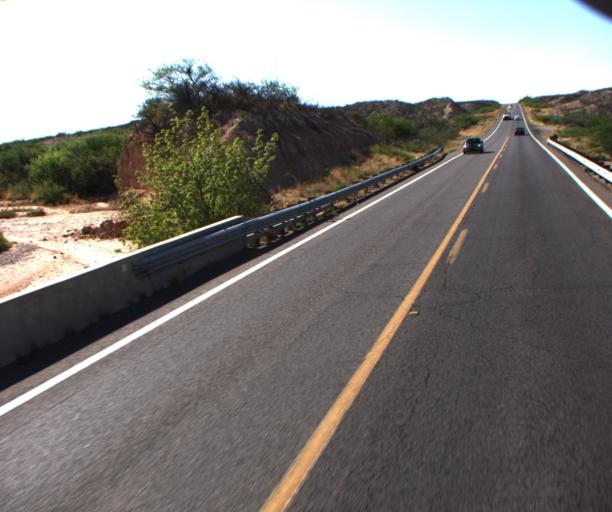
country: US
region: Arizona
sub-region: Cochise County
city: Saint David
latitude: 31.8145
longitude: -110.1658
